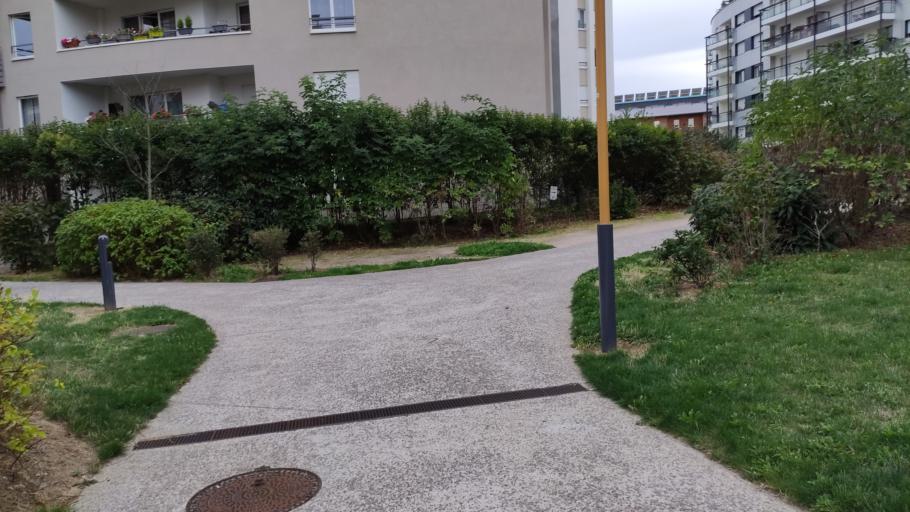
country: FR
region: Ile-de-France
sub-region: Departement des Hauts-de-Seine
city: Issy-les-Moulineaux
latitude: 48.8171
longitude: 2.2691
